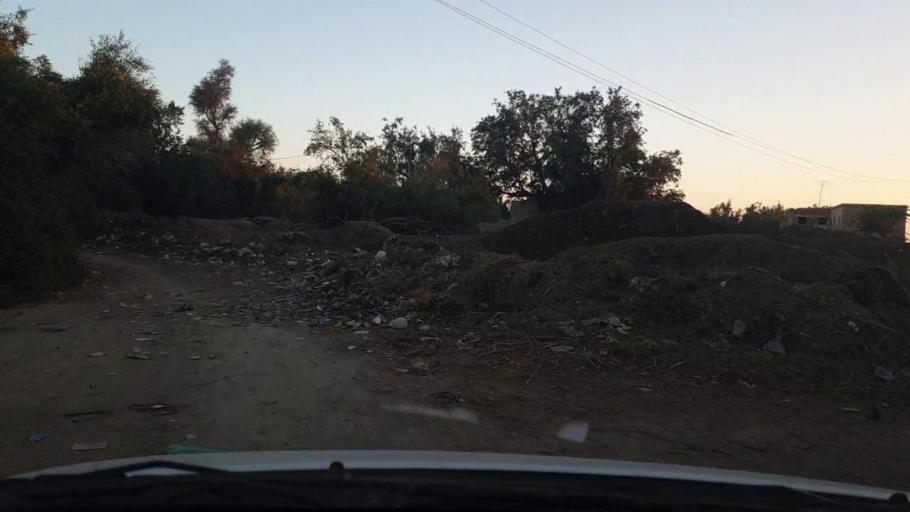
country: PK
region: Sindh
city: Johi
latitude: 26.8298
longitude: 67.4449
